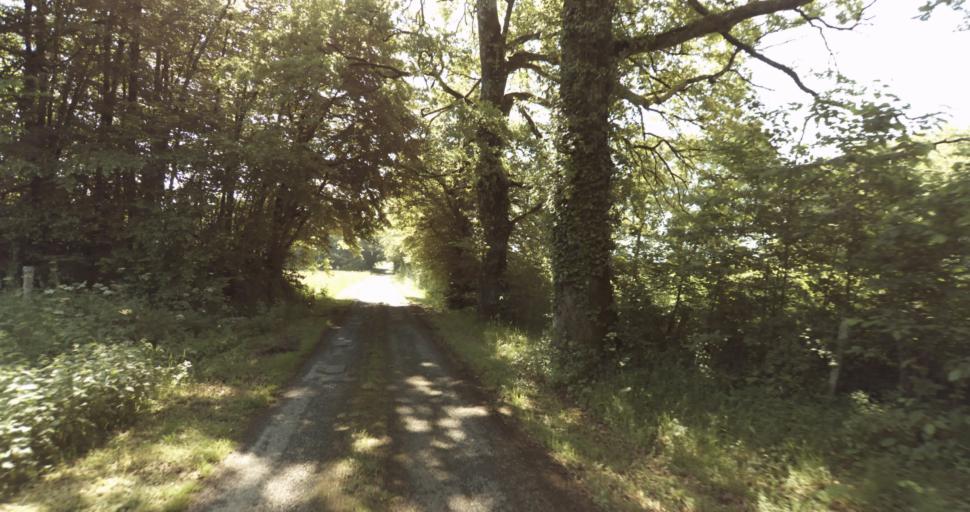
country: FR
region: Limousin
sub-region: Departement de la Haute-Vienne
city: Le Vigen
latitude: 45.7180
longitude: 1.2766
